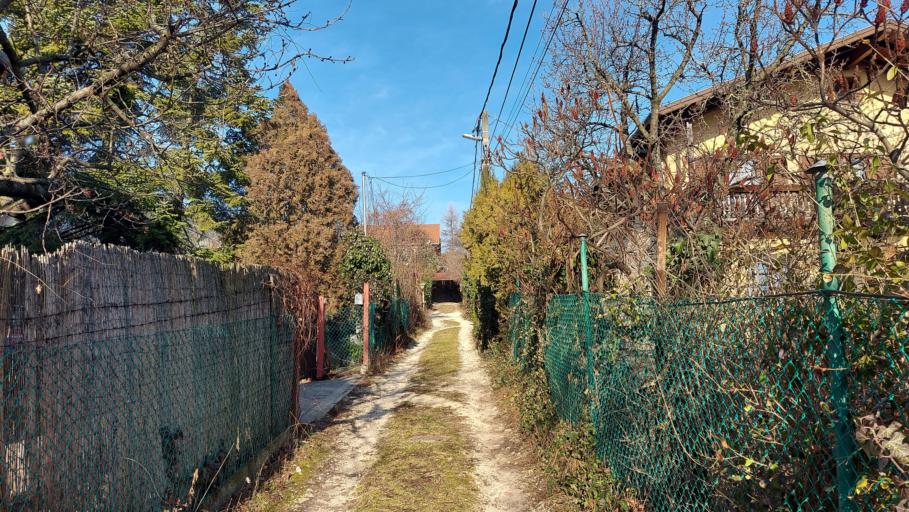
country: HU
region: Pest
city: Budaors
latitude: 47.4614
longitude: 18.9261
